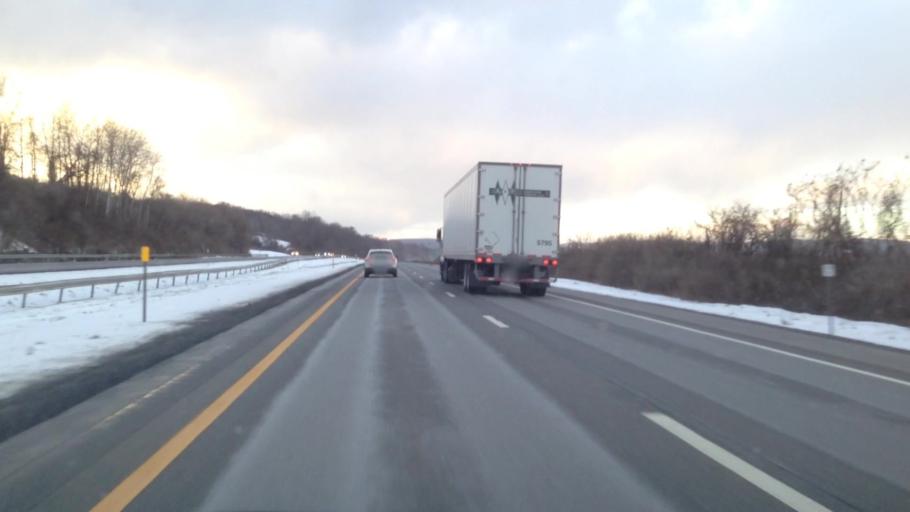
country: US
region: New York
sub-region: Herkimer County
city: Little Falls
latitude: 43.0066
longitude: -74.8978
